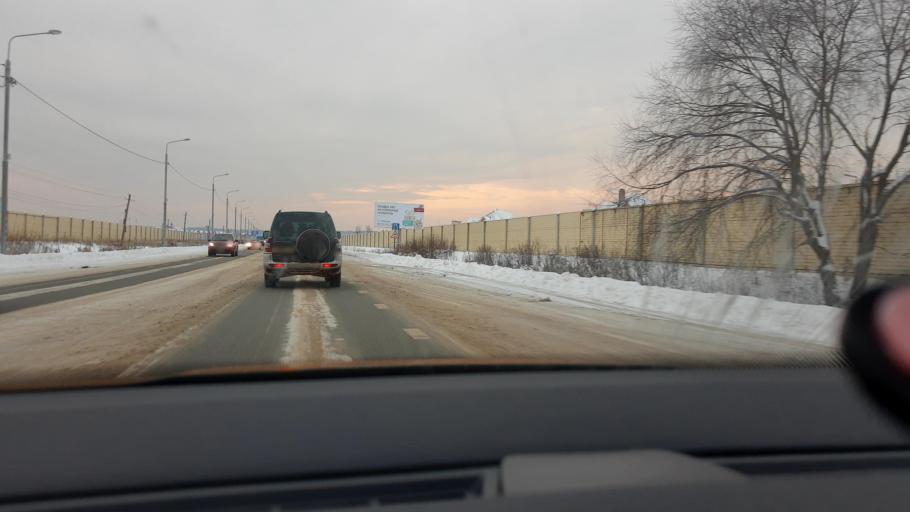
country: RU
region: Moskovskaya
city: Rozhdestveno
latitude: 55.8110
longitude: 37.0013
